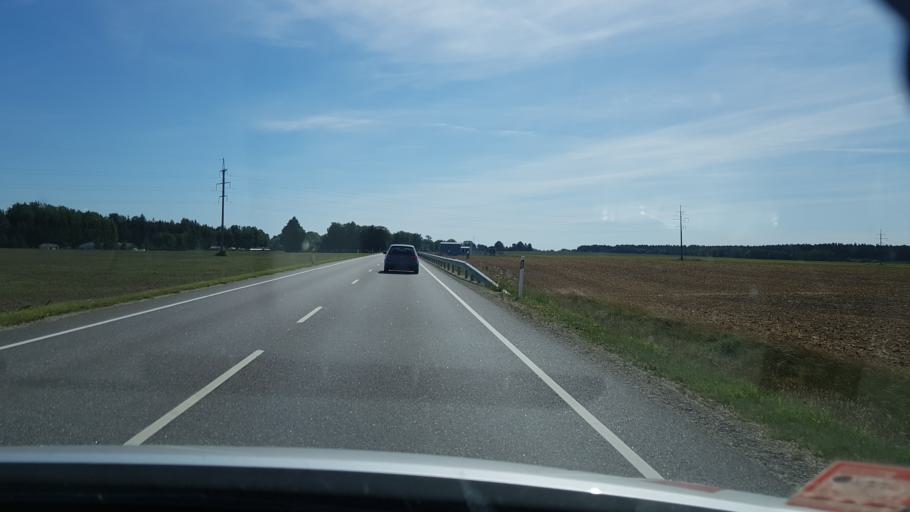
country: EE
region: Tartu
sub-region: Tartu linn
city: Tartu
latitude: 58.4175
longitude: 26.8773
